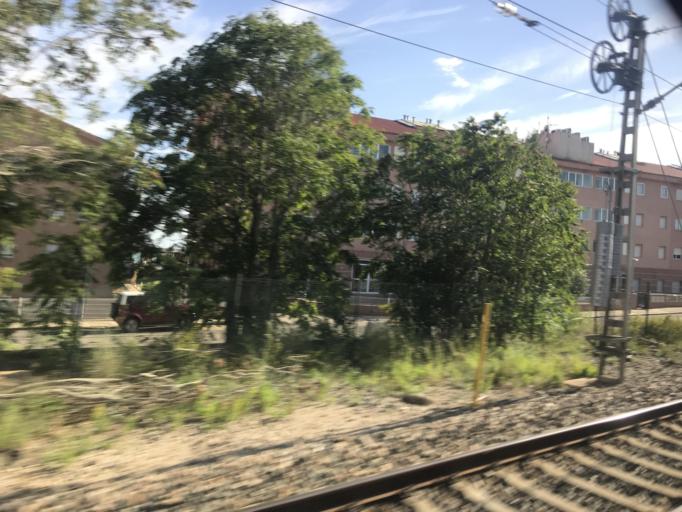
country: ES
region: Catalonia
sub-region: Provincia de Tarragona
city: L'Ampolla
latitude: 40.8094
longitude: 0.7042
